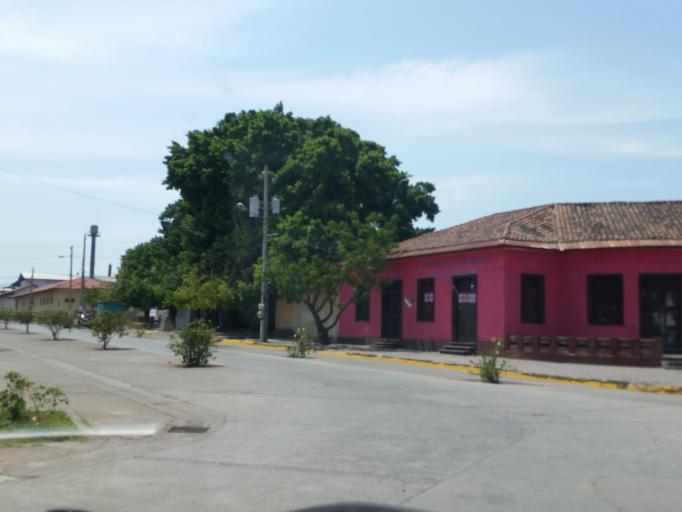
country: NI
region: Granada
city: Granada
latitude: 11.9377
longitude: -85.9554
